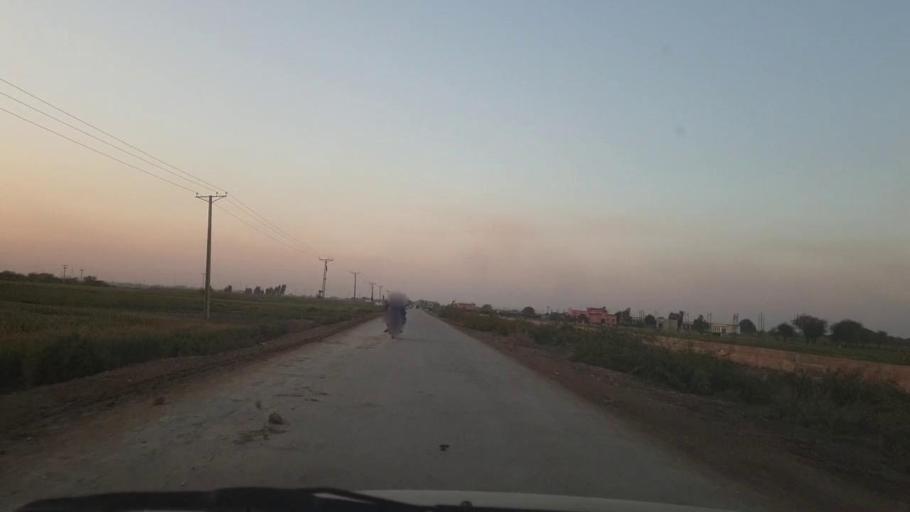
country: PK
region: Sindh
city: Mirpur Khas
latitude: 25.4917
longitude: 69.0396
